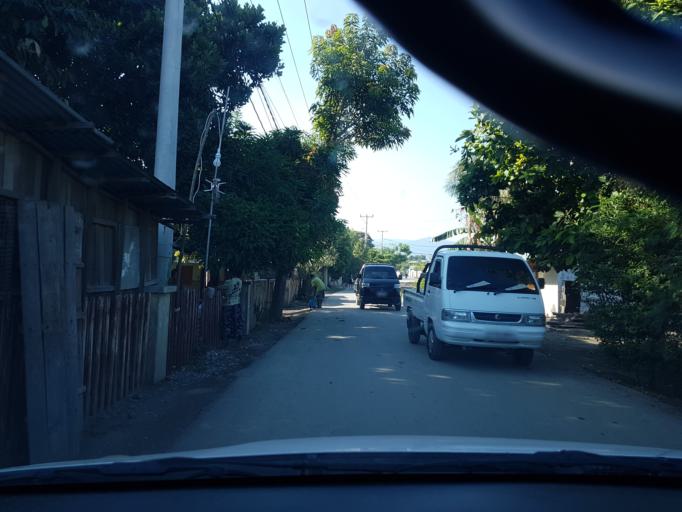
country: TL
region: Dili
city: Dili
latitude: -8.5431
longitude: 125.5416
